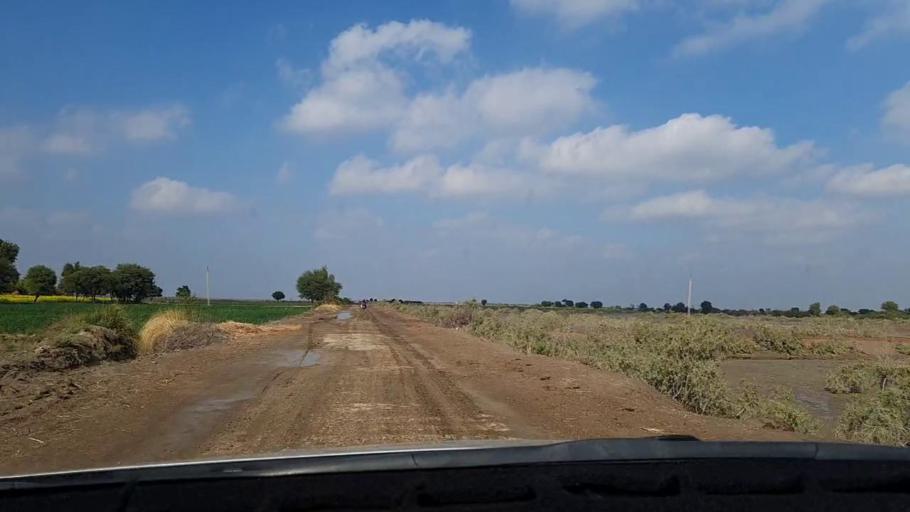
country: PK
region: Sindh
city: Tando Mittha Khan
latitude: 25.7788
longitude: 69.2560
